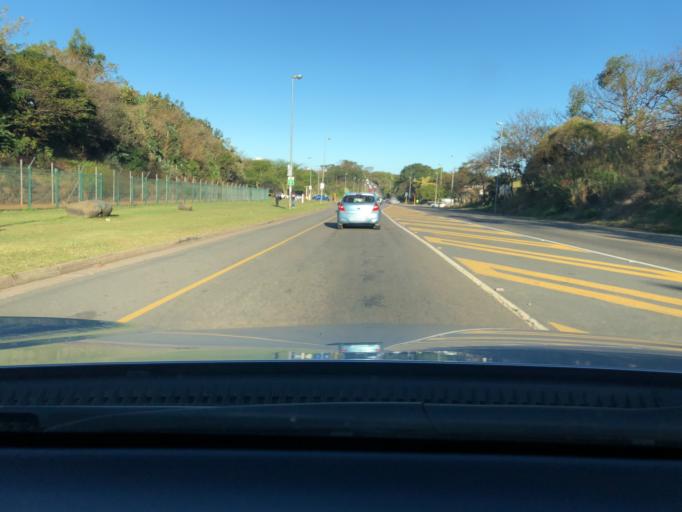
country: ZA
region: KwaZulu-Natal
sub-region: eThekwini Metropolitan Municipality
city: Umkomaas
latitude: -30.0320
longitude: 30.8887
